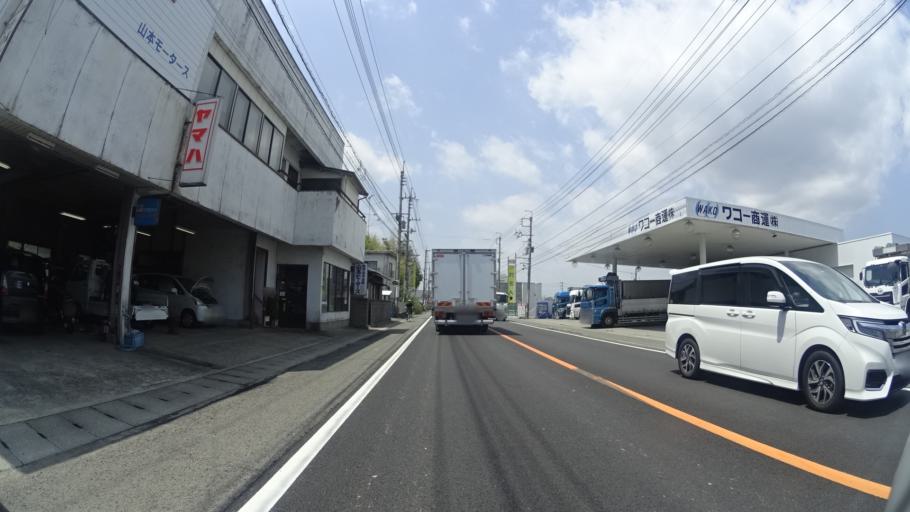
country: JP
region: Tokushima
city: Ishii
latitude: 34.0704
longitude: 134.4643
